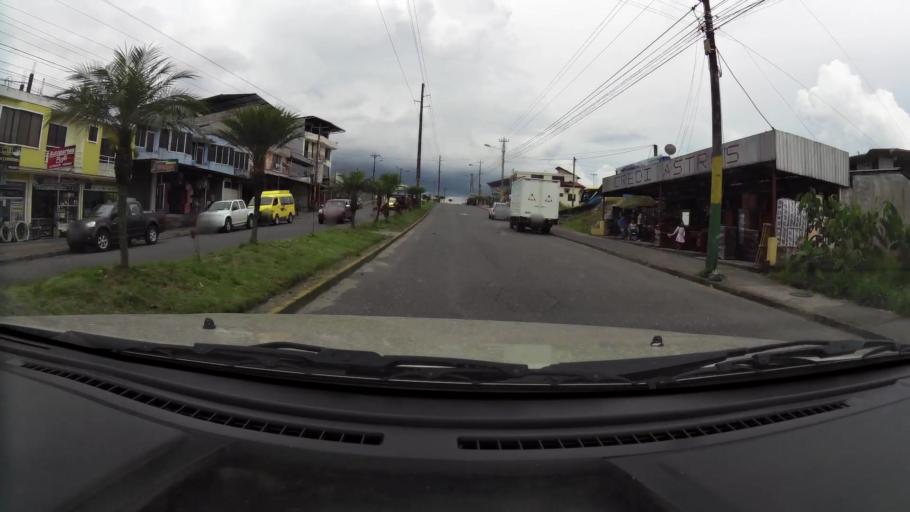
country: EC
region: Pastaza
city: Puyo
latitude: -1.4905
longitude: -78.0089
